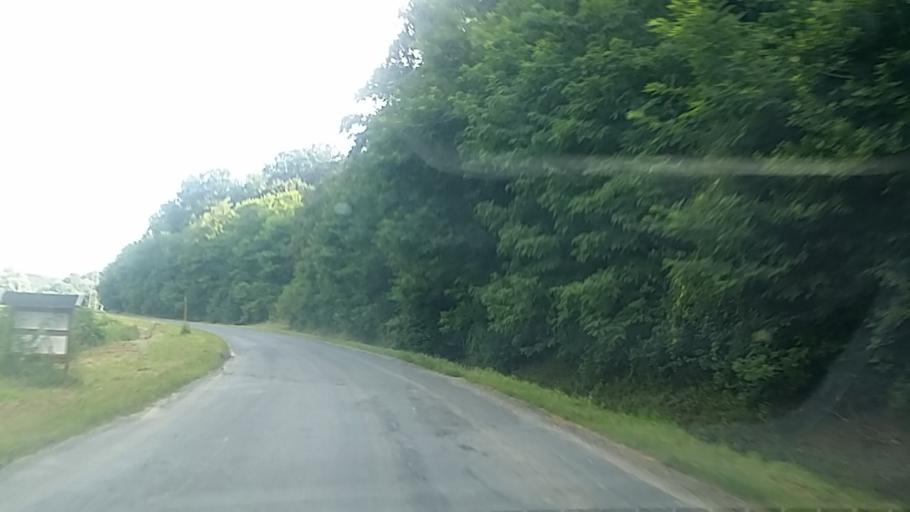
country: HU
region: Zala
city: Lenti
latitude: 46.5474
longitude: 16.5918
